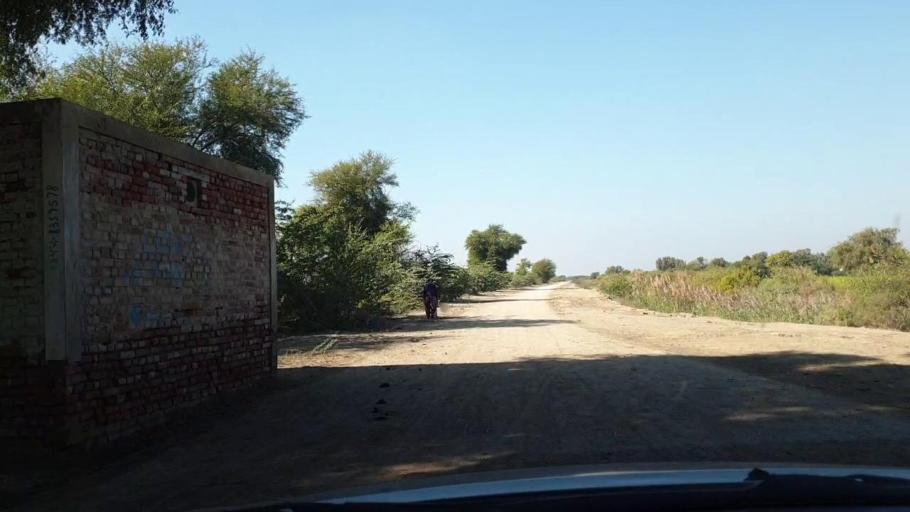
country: PK
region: Sindh
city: Jhol
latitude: 25.9199
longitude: 68.9617
